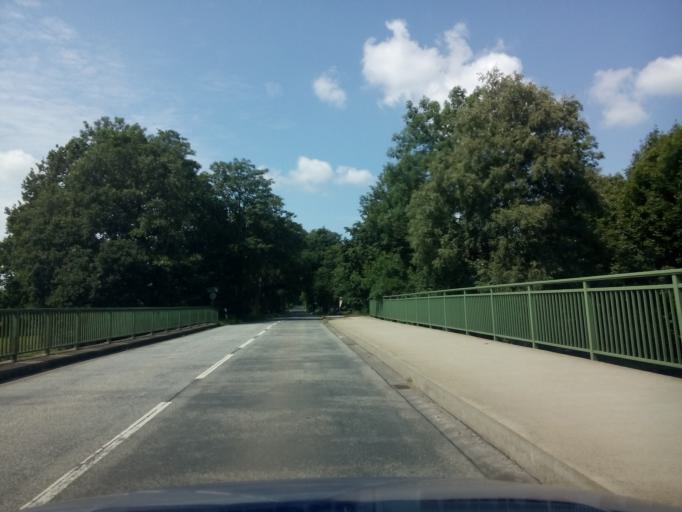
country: DE
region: Lower Saxony
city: Worpswede
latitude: 53.2643
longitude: 8.9171
